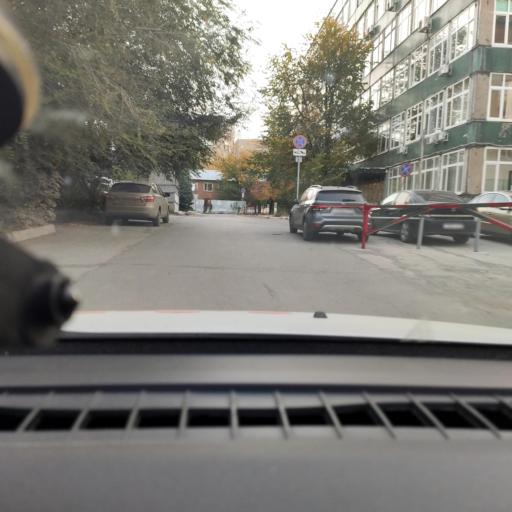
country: RU
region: Samara
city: Samara
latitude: 53.2103
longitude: 50.1250
